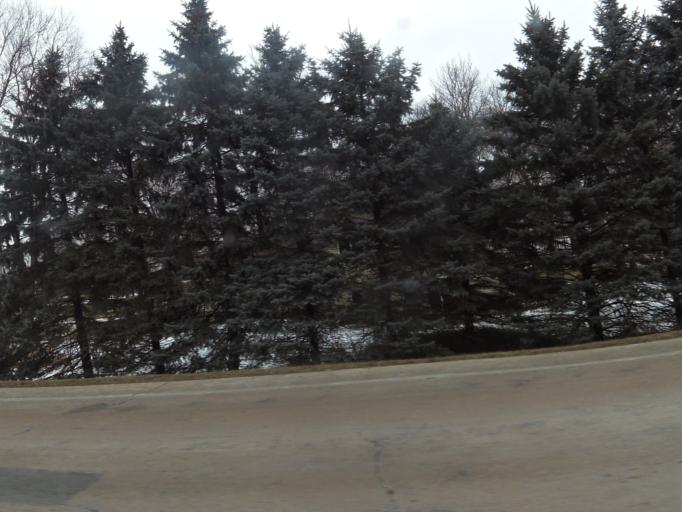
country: US
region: Minnesota
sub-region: Carver County
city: Waconia
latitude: 44.8551
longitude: -93.8028
